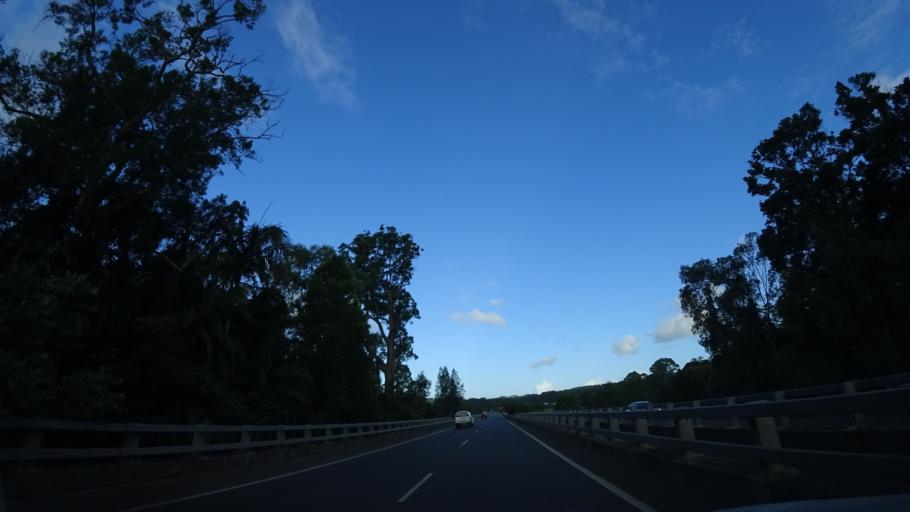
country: AU
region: Queensland
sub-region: Sunshine Coast
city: Woombye
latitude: -26.6715
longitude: 153.0100
